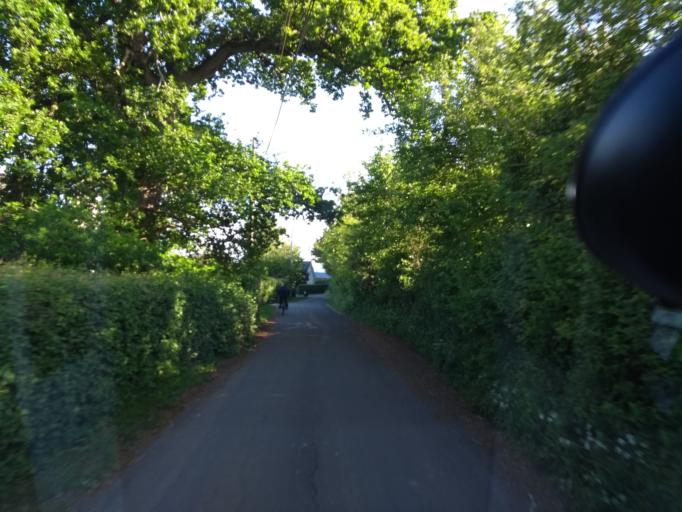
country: GB
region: England
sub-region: Somerset
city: Creech Saint Michael
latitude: 51.0006
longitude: -3.0525
